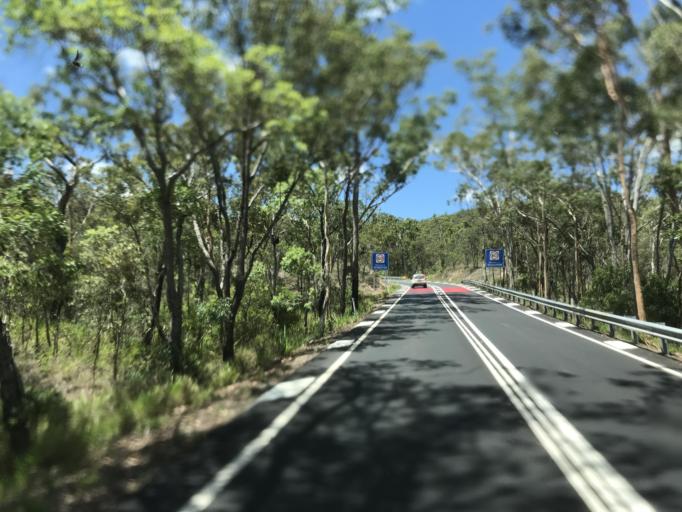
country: AU
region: Queensland
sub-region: Tablelands
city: Atherton
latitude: -17.4002
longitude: 145.3899
